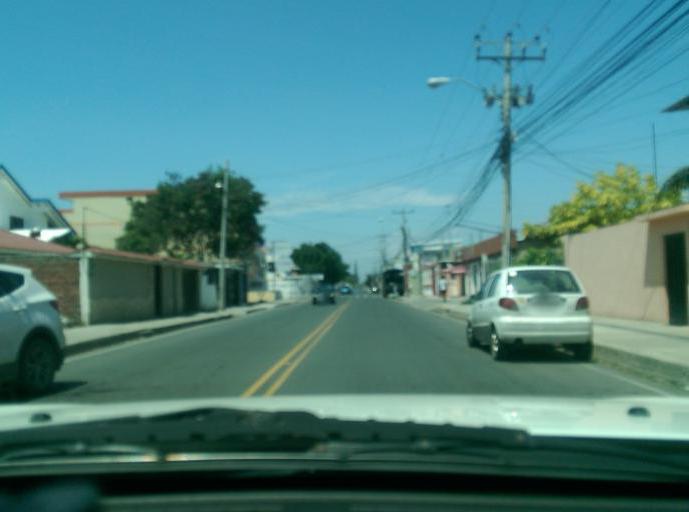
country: EC
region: Manabi
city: Manta
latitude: -0.9573
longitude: -80.7536
